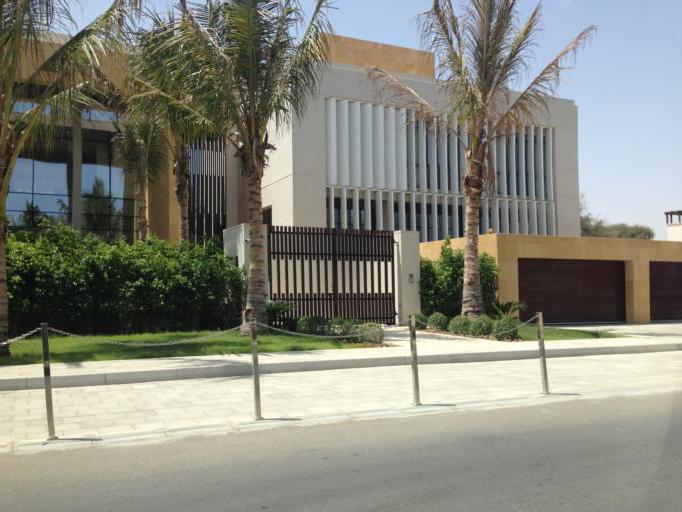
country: OM
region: Muhafazat Masqat
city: Bawshar
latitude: 23.6039
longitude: 58.3640
